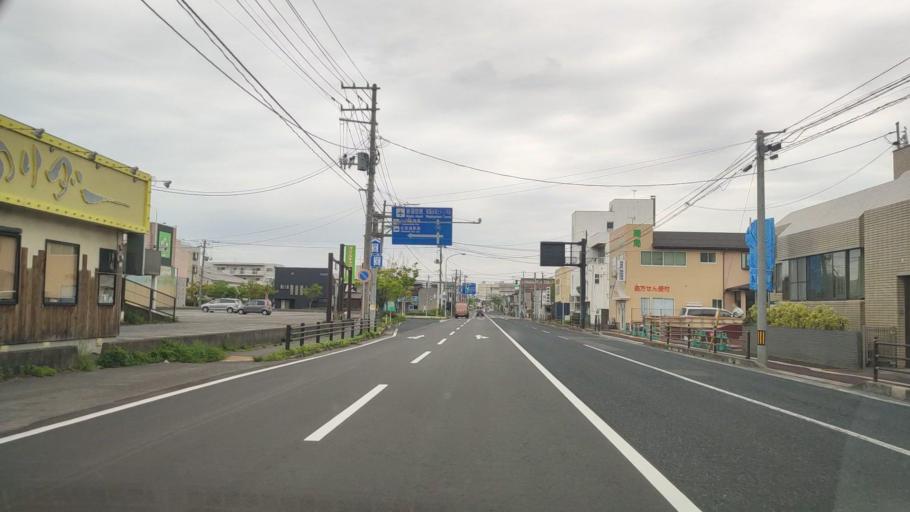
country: JP
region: Niigata
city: Niigata-shi
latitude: 37.9352
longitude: 139.0725
